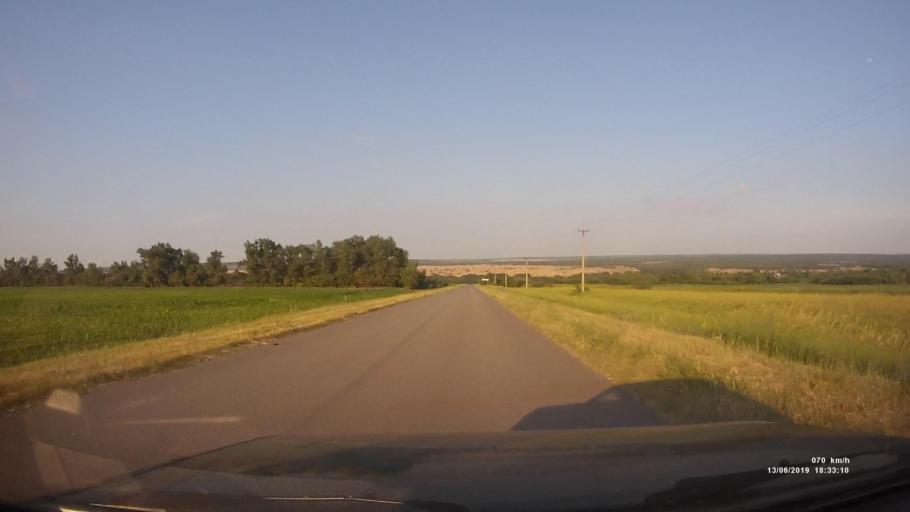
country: RU
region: Rostov
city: Kazanskaya
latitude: 49.8703
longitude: 41.3782
